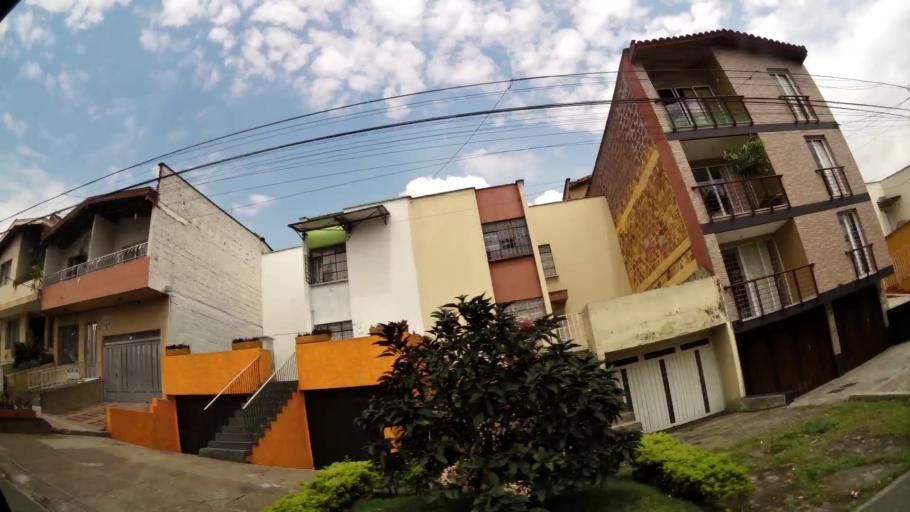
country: CO
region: Antioquia
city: Medellin
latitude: 6.2486
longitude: -75.6142
